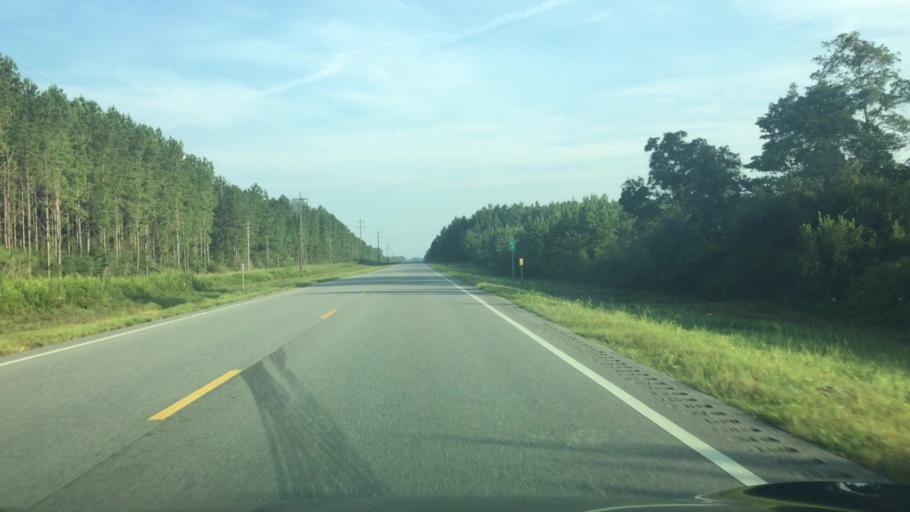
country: US
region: Alabama
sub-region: Covington County
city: Florala
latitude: 31.0269
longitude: -86.3684
